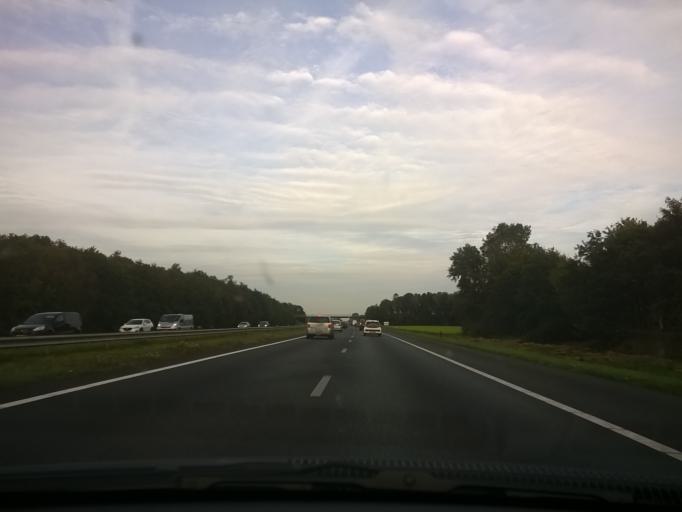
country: NL
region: Friesland
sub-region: Gemeente Achtkarspelen
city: Surhuisterveen
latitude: 53.1376
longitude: 6.2132
